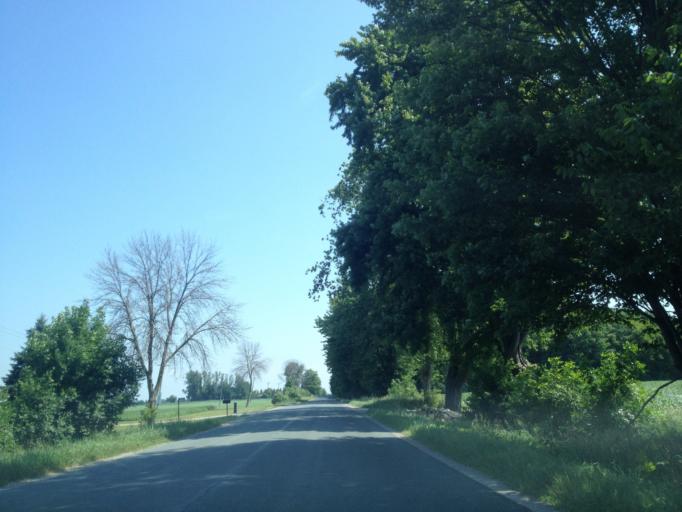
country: CA
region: Ontario
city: Stratford
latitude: 43.2601
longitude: -81.2036
